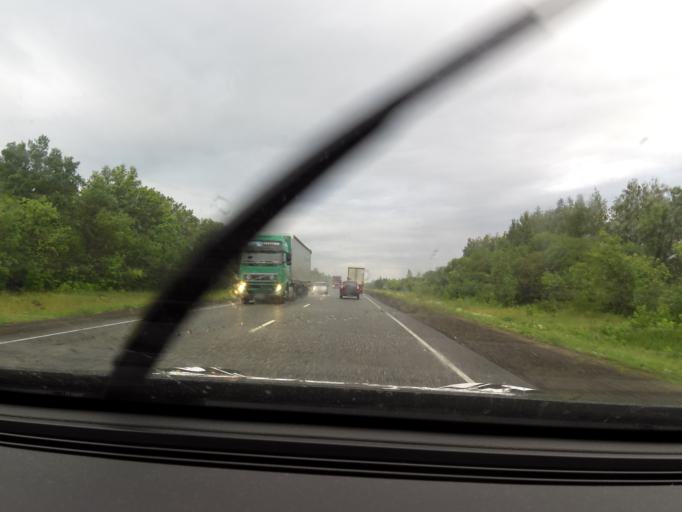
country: RU
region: Chuvashia
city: Kozlovka
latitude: 55.7971
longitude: 48.1000
